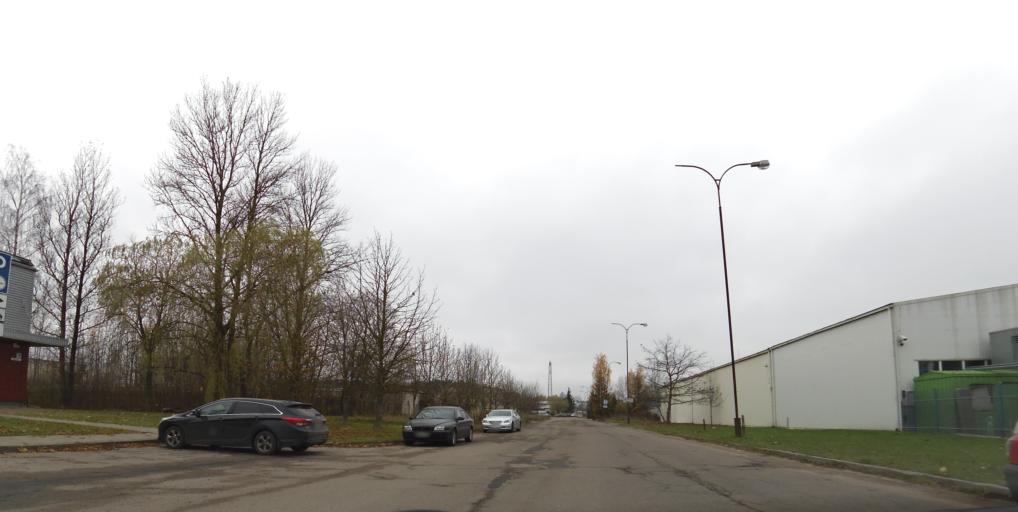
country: LT
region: Vilnius County
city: Vilkpede
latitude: 54.6343
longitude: 25.2650
